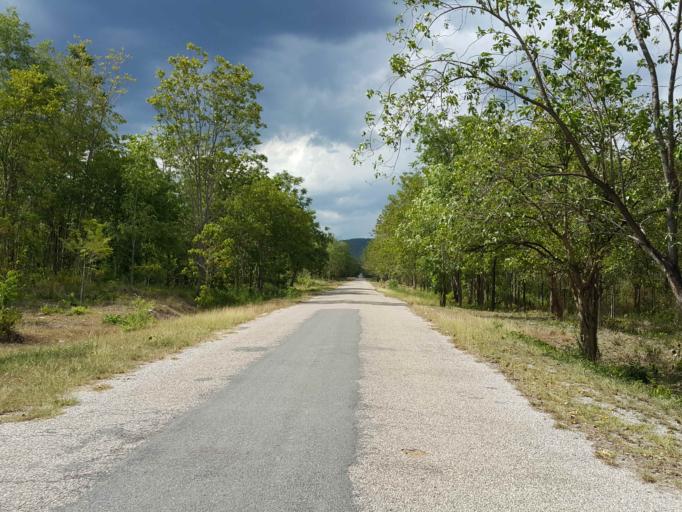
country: TH
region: Sukhothai
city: Thung Saliam
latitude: 17.3342
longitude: 99.4239
